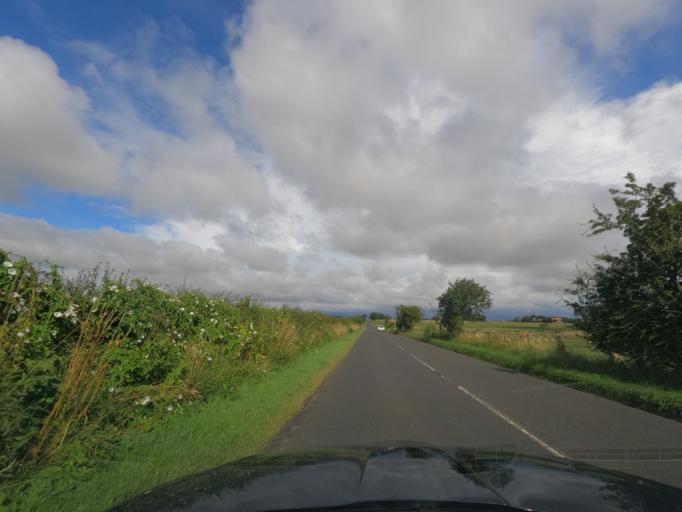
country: GB
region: England
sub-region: Northumberland
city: Lowick
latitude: 55.6359
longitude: -1.9908
